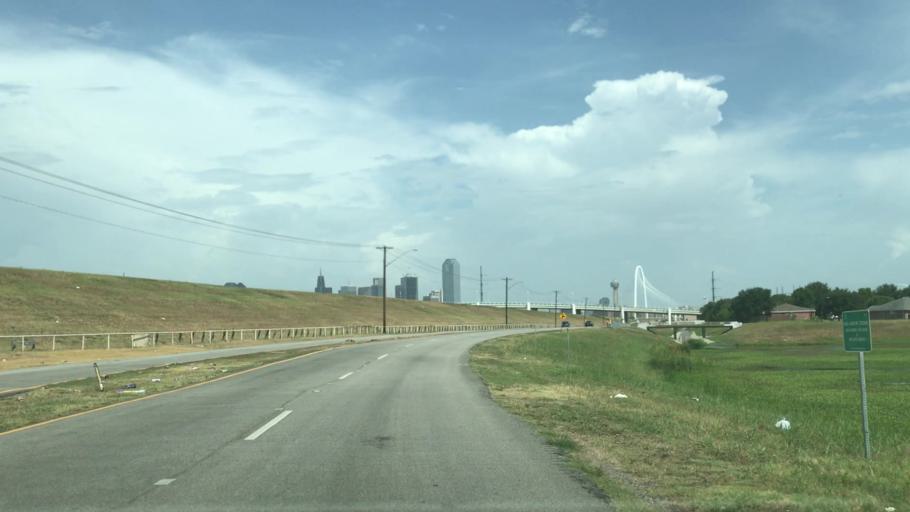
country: US
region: Texas
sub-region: Dallas County
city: Dallas
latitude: 32.7886
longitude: -96.8420
